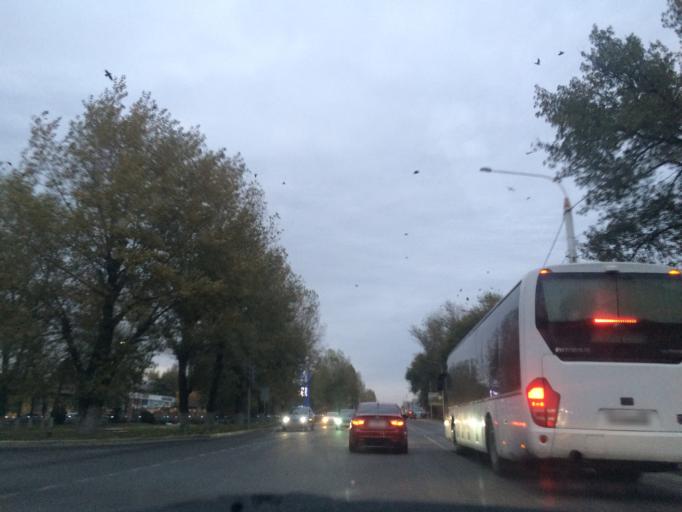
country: RU
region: Rostov
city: Novocherkassk
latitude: 47.4210
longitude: 40.0417
